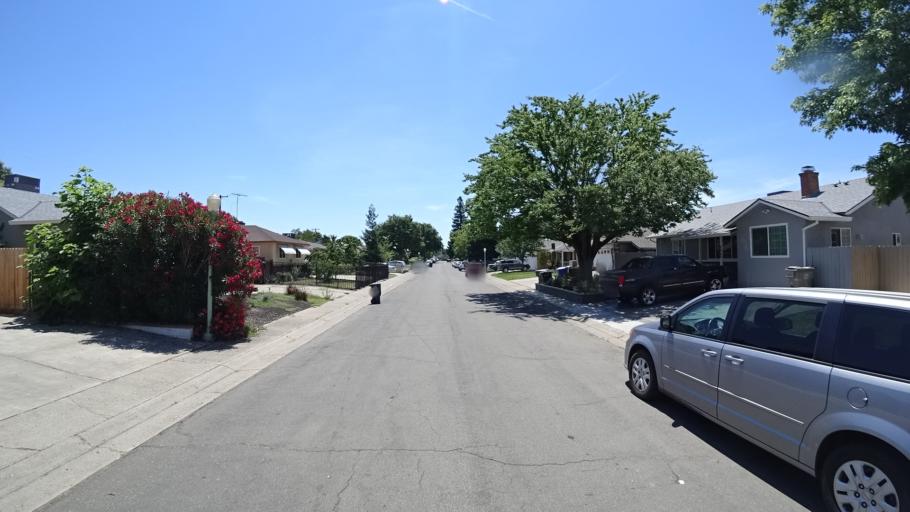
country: US
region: California
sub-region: Sacramento County
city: Florin
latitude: 38.5316
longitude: -121.4176
